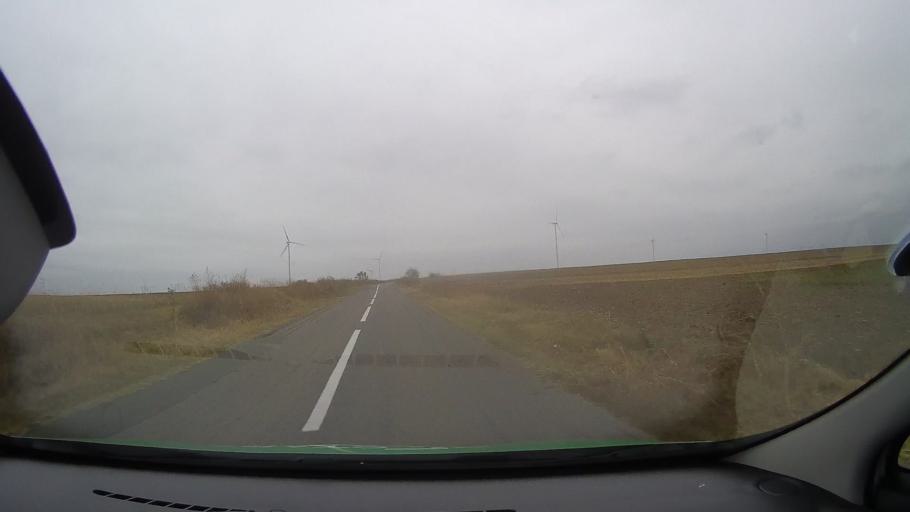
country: RO
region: Constanta
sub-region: Comuna Pantelimon
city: Pantelimon
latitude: 44.5015
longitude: 28.3537
